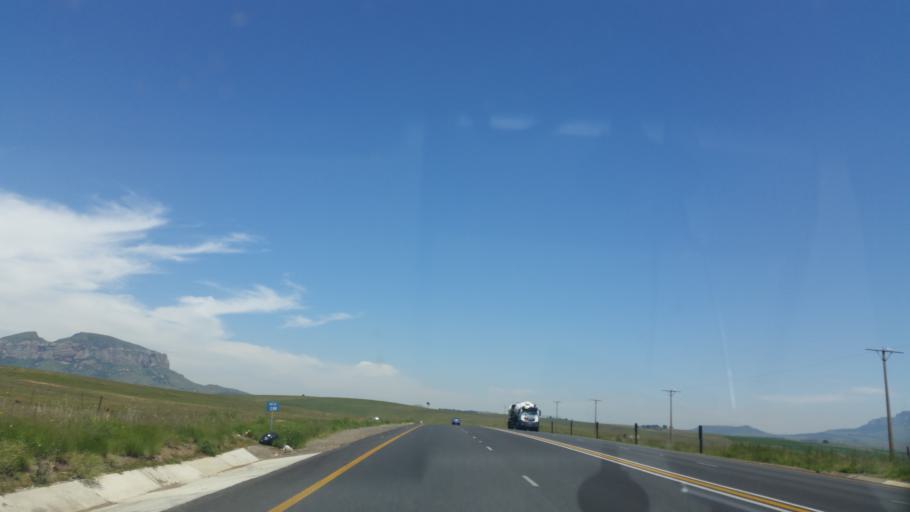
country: ZA
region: Orange Free State
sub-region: Thabo Mofutsanyana District Municipality
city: Harrismith
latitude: -28.3665
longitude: 29.3460
